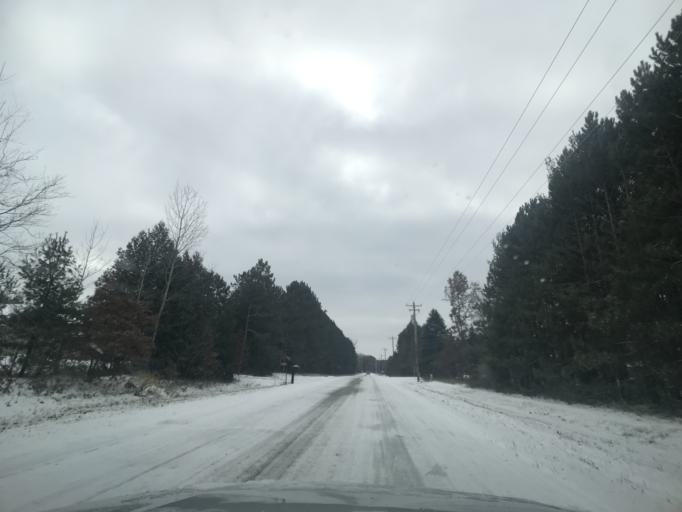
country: US
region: Wisconsin
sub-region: Brown County
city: Suamico
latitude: 44.6959
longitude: -88.1008
